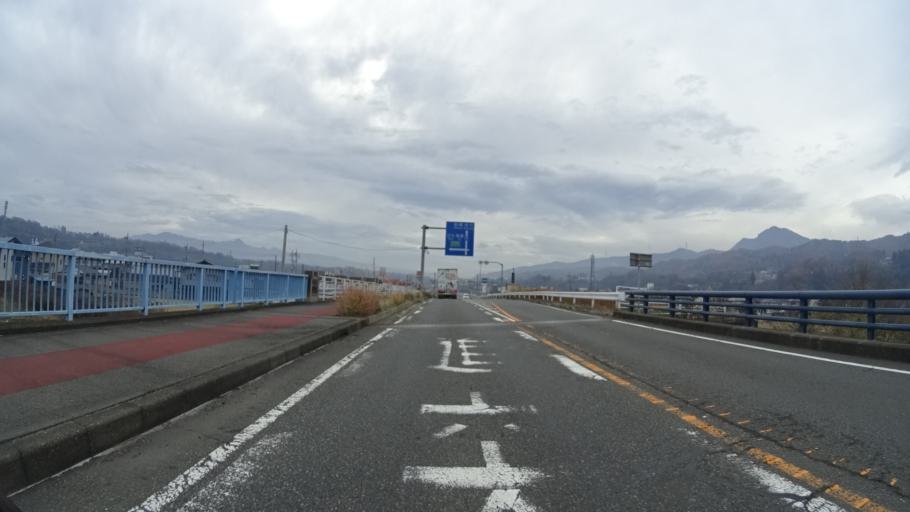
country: JP
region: Gunma
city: Numata
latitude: 36.6459
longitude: 139.0281
